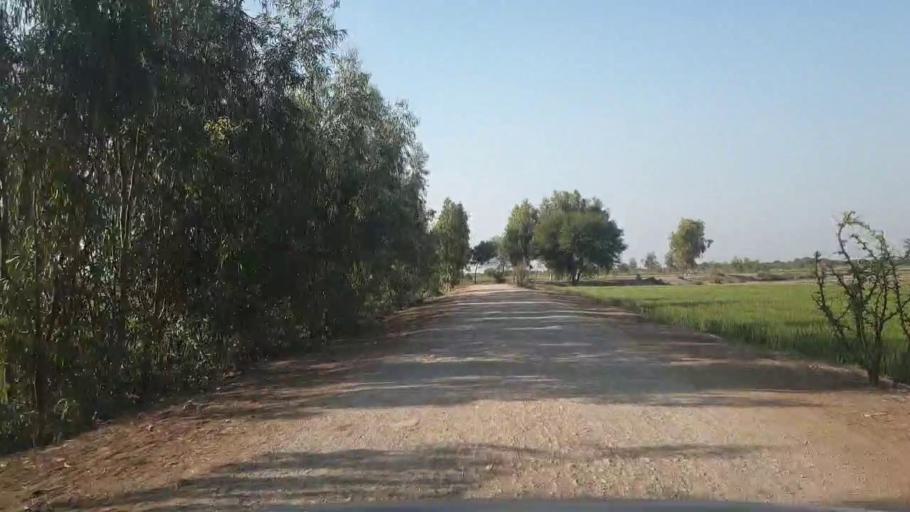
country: PK
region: Sindh
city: Chambar
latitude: 25.2951
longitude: 68.8634
